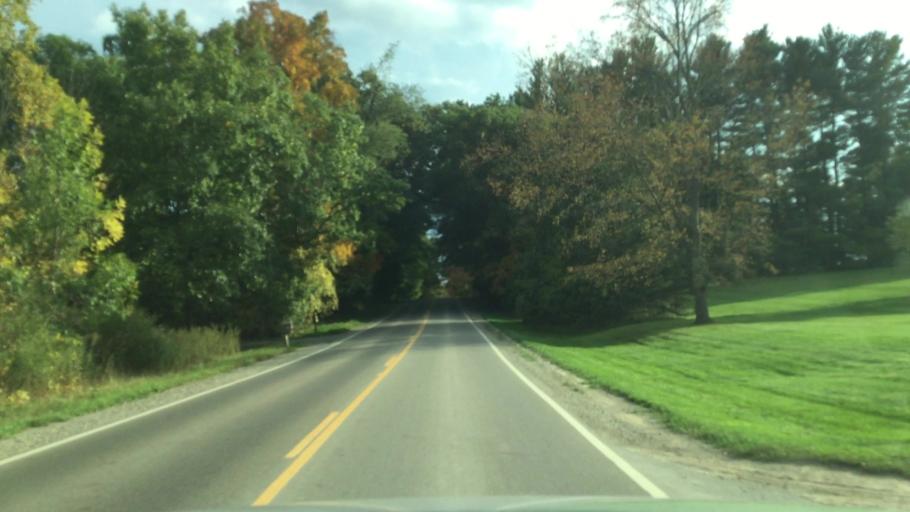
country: US
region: Michigan
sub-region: Genesee County
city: Fenton
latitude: 42.6770
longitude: -83.7021
